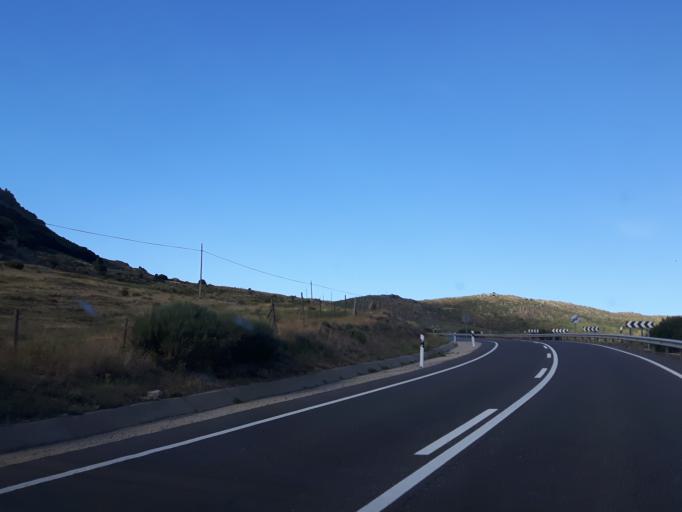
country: ES
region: Castille and Leon
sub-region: Provincia de Avila
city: Mengamunoz
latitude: 40.4950
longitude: -5.0043
